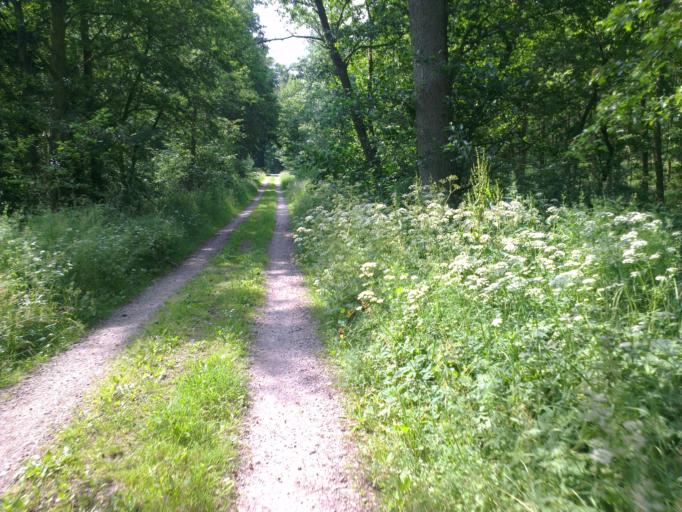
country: DK
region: Capital Region
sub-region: Allerod Kommune
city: Lillerod
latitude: 55.9042
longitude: 12.3568
